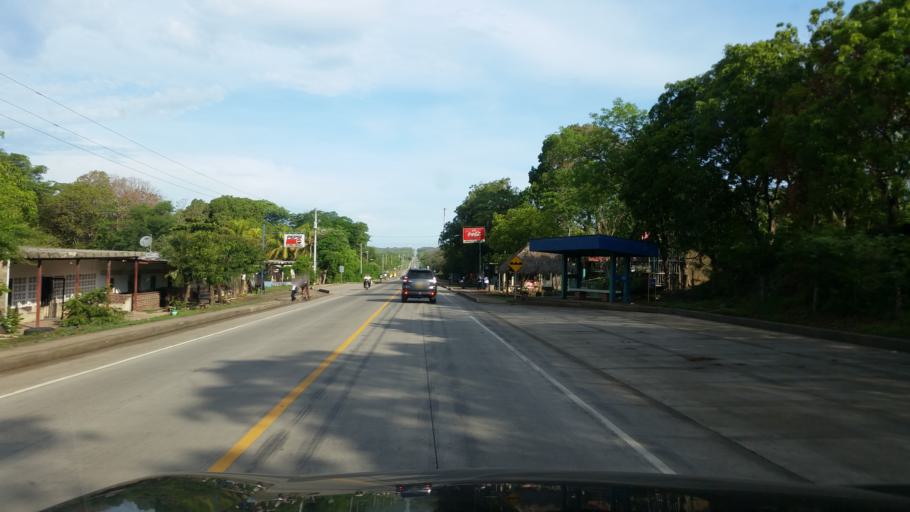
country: NI
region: Managua
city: Carlos Fonseca Amador
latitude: 12.1087
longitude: -86.5937
